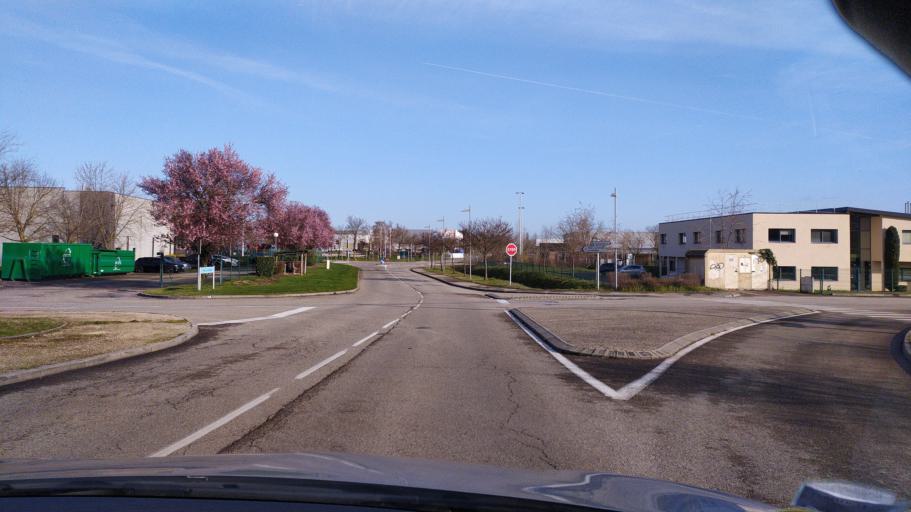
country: FR
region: Rhone-Alpes
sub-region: Departement de l'Isere
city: Saint-Quentin-Fallavier
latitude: 45.6385
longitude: 5.1152
